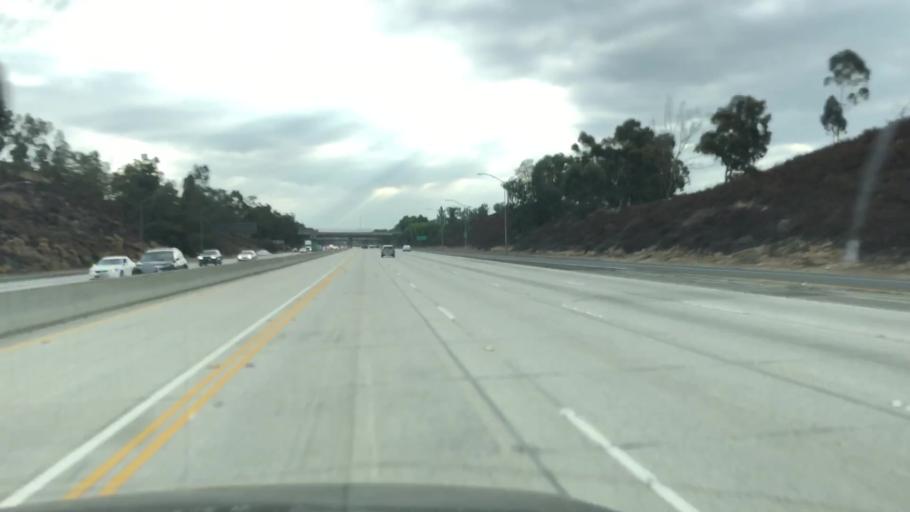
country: US
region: California
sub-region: Los Angeles County
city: Chatsworth
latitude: 34.2734
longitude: -118.5875
